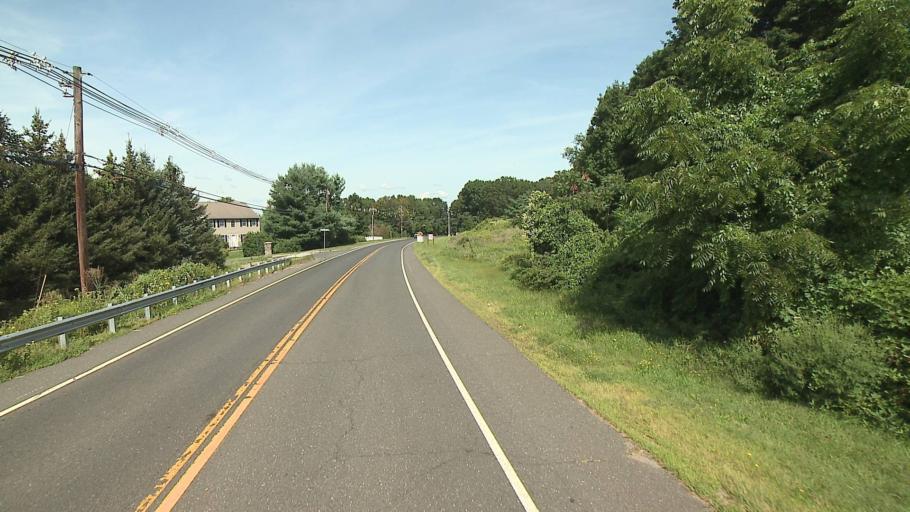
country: US
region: Connecticut
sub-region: Litchfield County
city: Watertown
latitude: 41.6173
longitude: -73.1030
